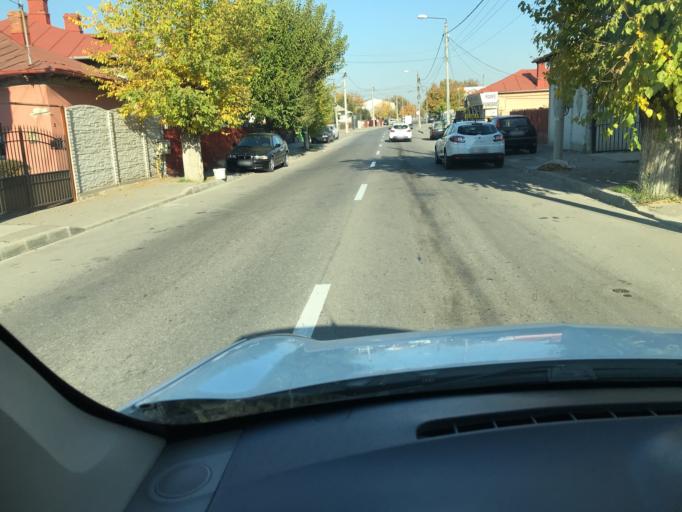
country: RO
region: Olt
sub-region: Municipiul Slatina
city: Slatina
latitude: 44.4329
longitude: 24.3519
